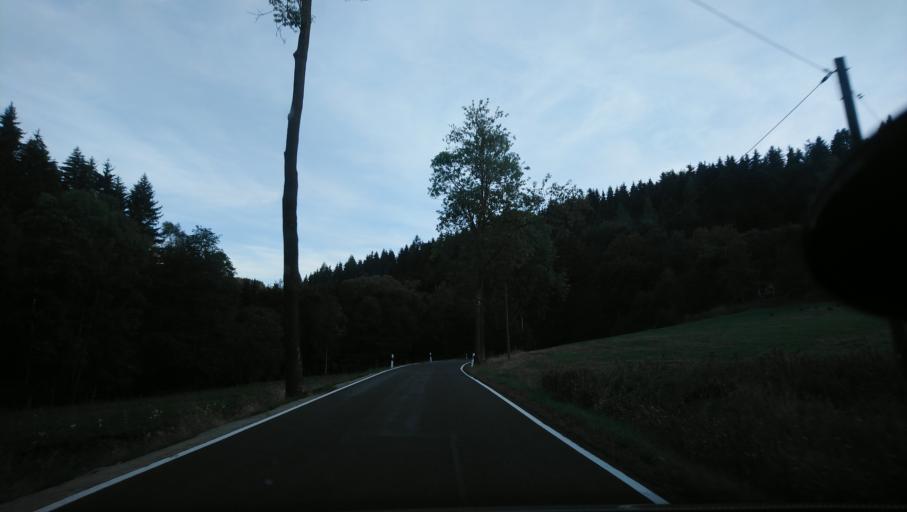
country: DE
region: Saxony
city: Barenstein
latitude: 50.5159
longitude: 13.0404
